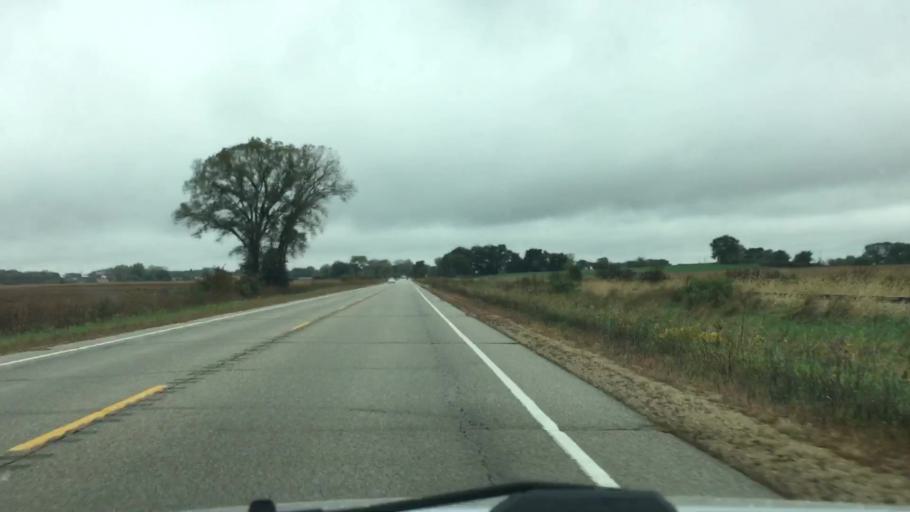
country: US
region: Wisconsin
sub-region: Walworth County
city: Whitewater
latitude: 42.7974
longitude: -88.8054
